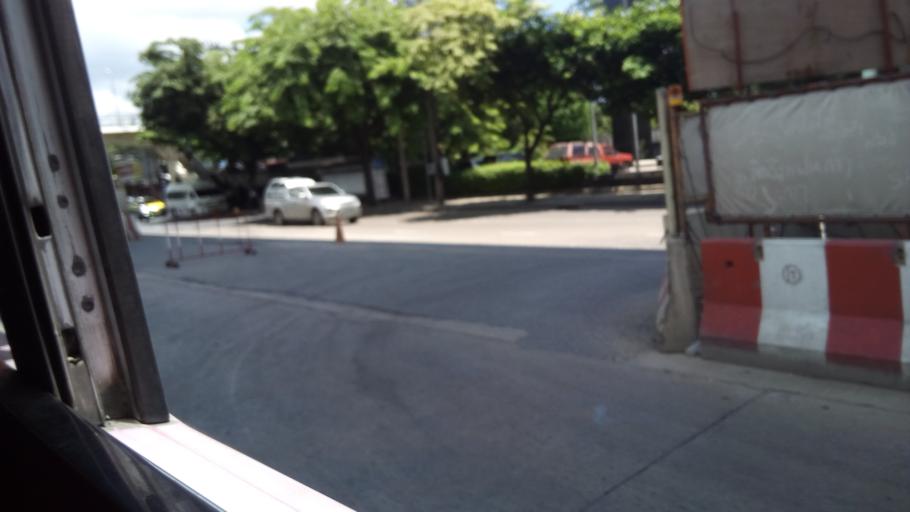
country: TH
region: Bangkok
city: Lak Si
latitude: 13.8548
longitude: 100.5846
